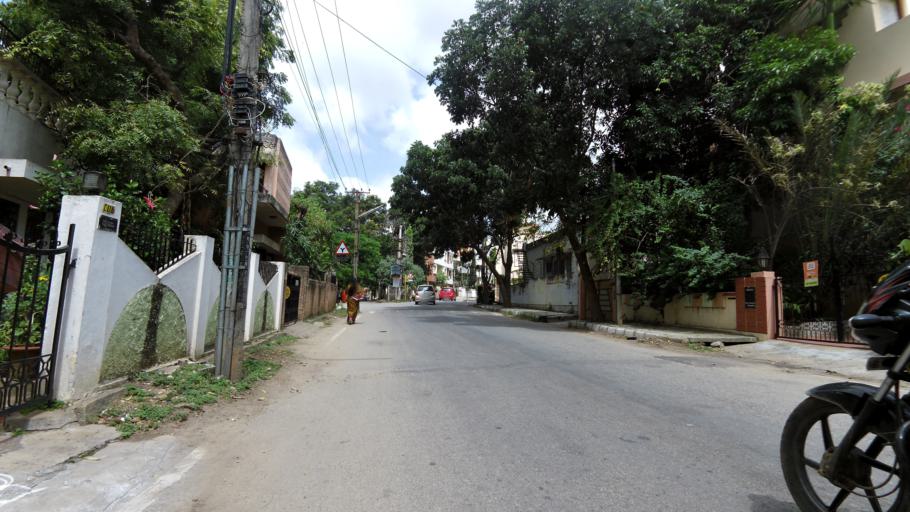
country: IN
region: Karnataka
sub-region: Bangalore Urban
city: Bangalore
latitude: 12.9938
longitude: 77.6272
